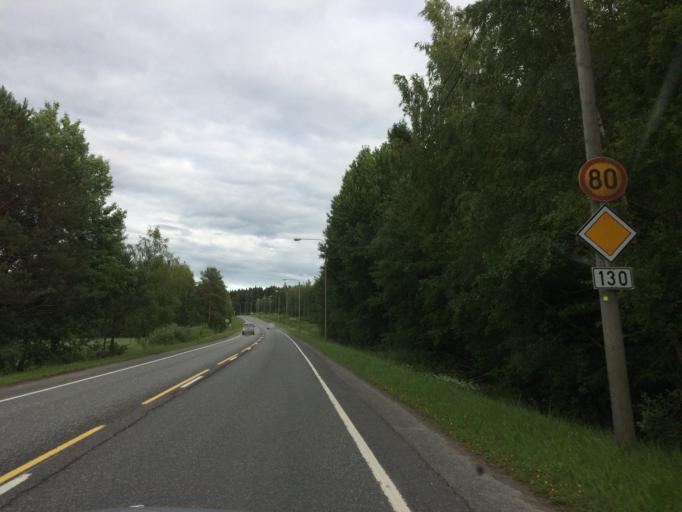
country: FI
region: Haeme
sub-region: Haemeenlinna
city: Haemeenlinna
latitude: 60.9591
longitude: 24.4862
